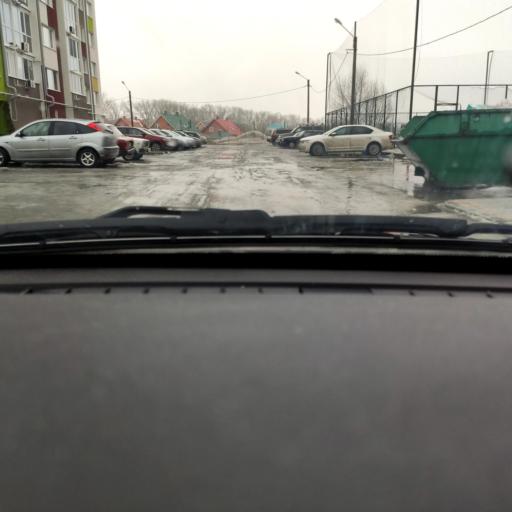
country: RU
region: Voronezj
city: Novaya Usman'
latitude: 51.6688
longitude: 39.4034
